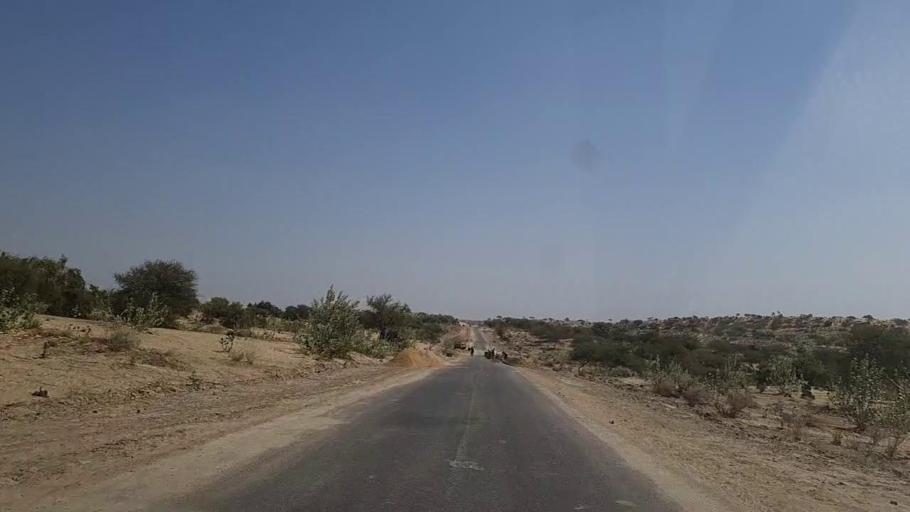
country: PK
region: Sindh
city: Diplo
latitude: 24.4839
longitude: 69.4699
